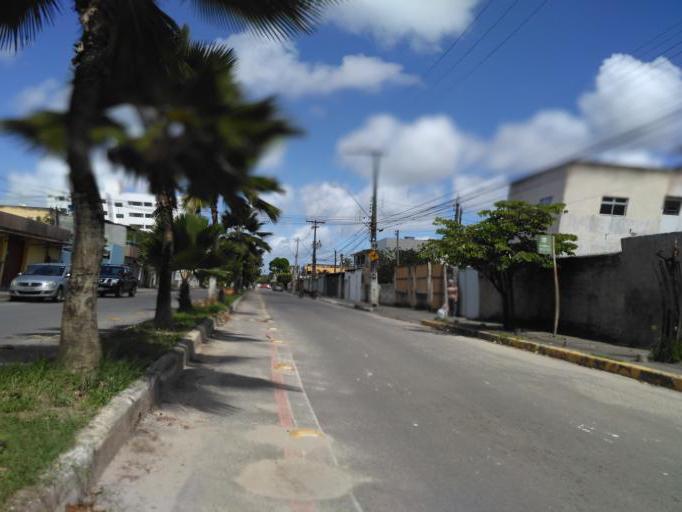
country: BR
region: Pernambuco
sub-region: Recife
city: Recife
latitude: -8.0493
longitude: -34.9356
